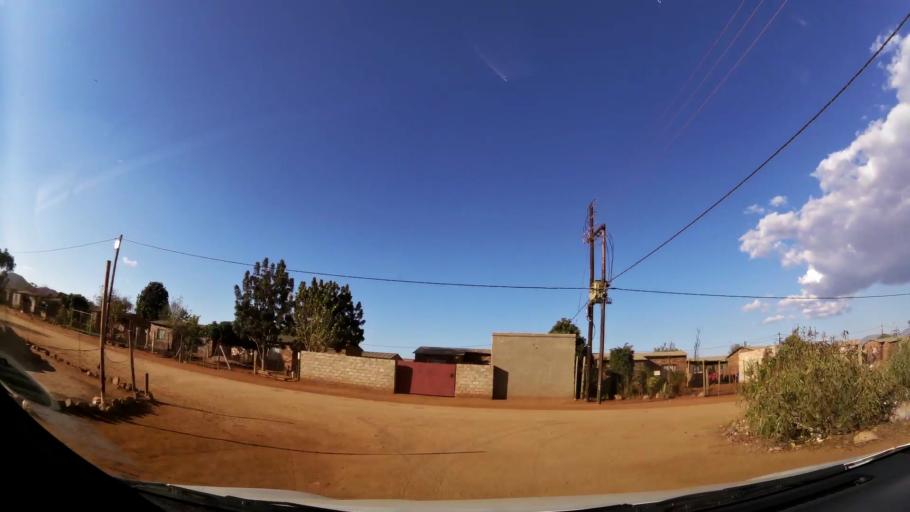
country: ZA
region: Limpopo
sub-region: Waterberg District Municipality
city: Mokopane
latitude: -24.1825
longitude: 28.9709
